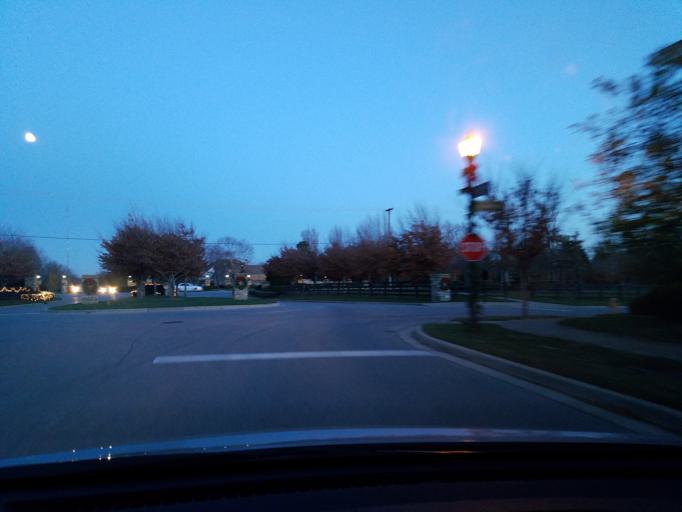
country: US
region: Kentucky
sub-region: Jefferson County
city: Worthington
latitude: 38.3245
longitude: -85.5624
